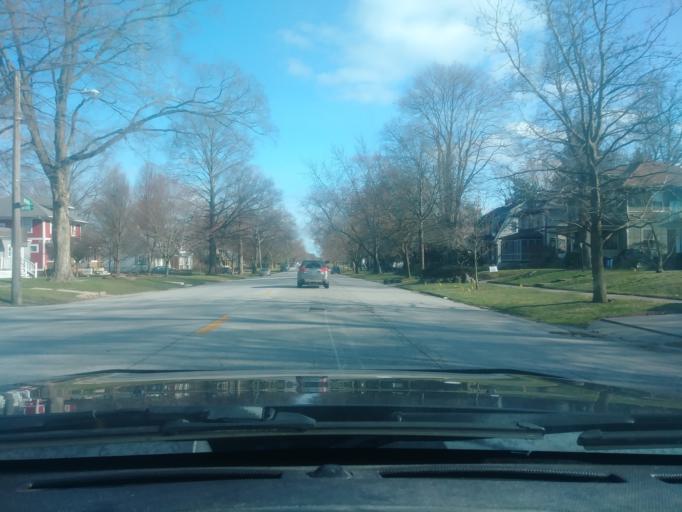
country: US
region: Indiana
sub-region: LaPorte County
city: LaPorte
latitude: 41.6001
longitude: -86.7127
